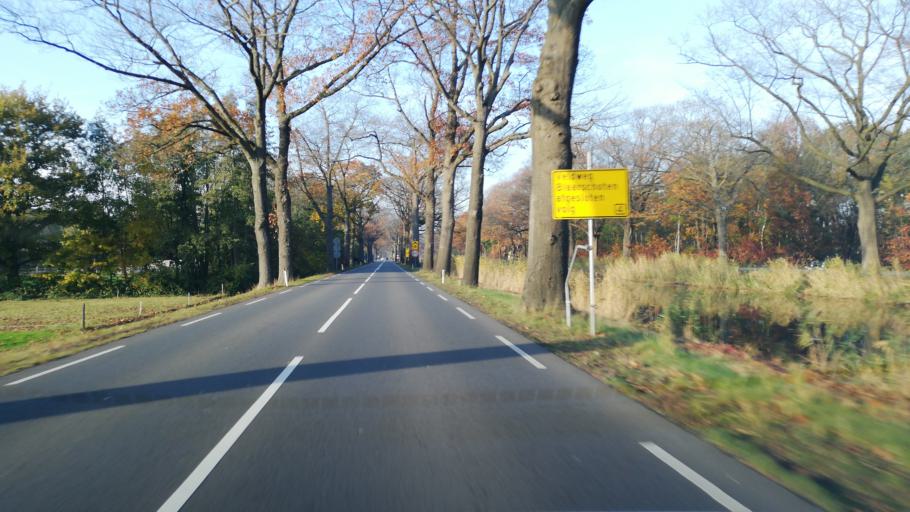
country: NL
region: Gelderland
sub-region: Gemeente Apeldoorn
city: Beekbergen
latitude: 52.1696
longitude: 5.9979
